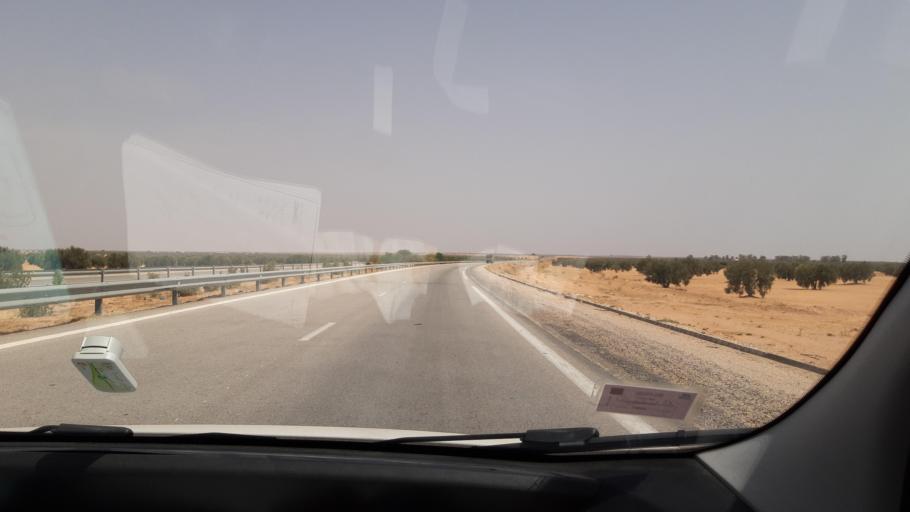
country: TN
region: Safaqis
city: Bi'r `Ali Bin Khalifah
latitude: 34.5313
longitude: 10.0982
